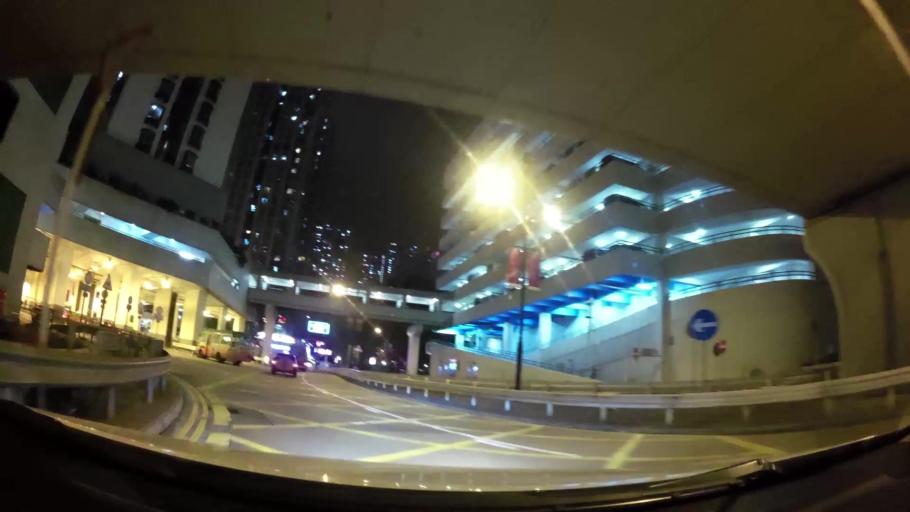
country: HK
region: Tsuen Wan
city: Tsuen Wan
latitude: 22.3560
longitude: 114.1271
